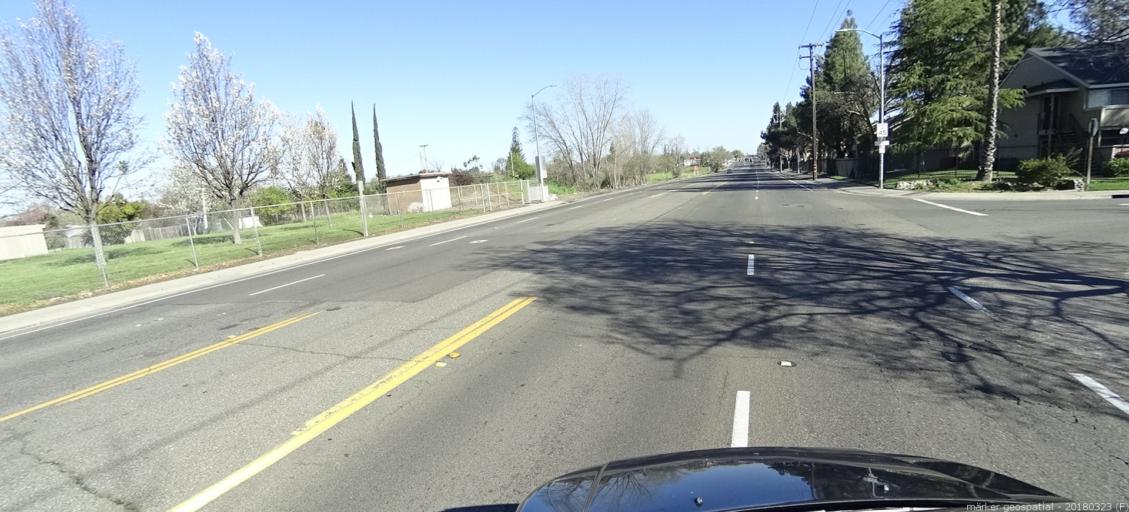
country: US
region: California
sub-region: Sacramento County
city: North Highlands
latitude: 38.6900
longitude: -121.3637
